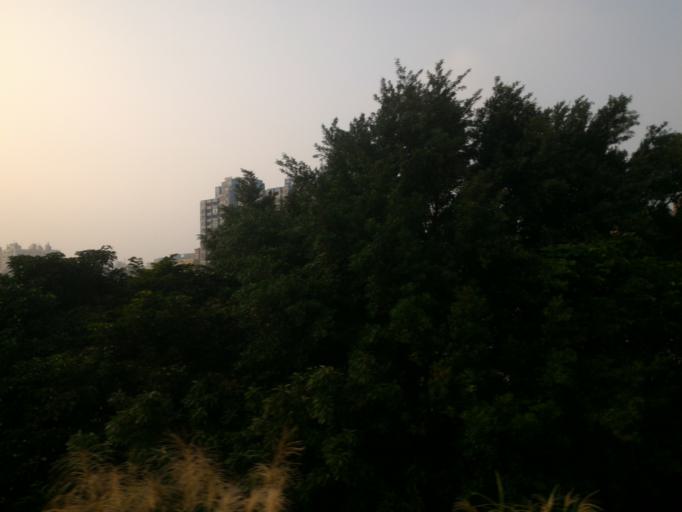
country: TW
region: Taiwan
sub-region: Taoyuan
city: Taoyuan
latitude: 24.9519
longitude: 121.3513
